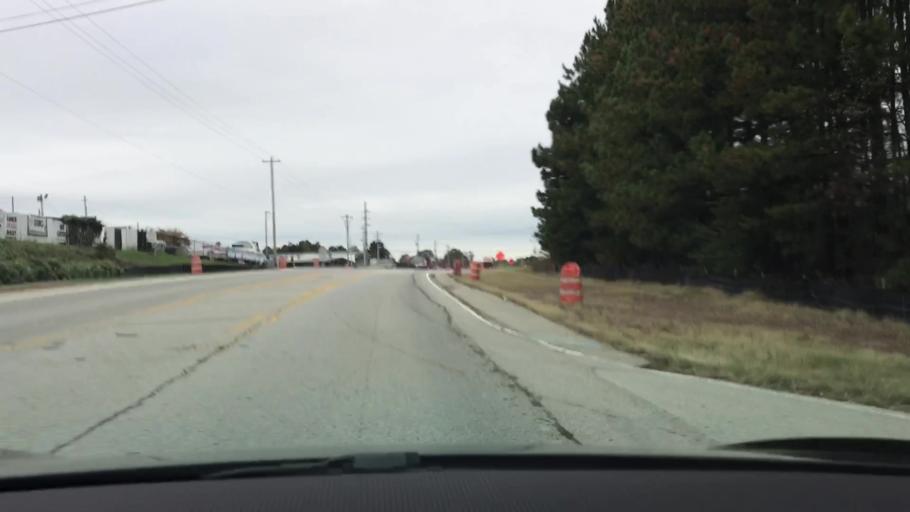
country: US
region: Georgia
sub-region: Gwinnett County
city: Buford
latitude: 34.1512
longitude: -83.9822
